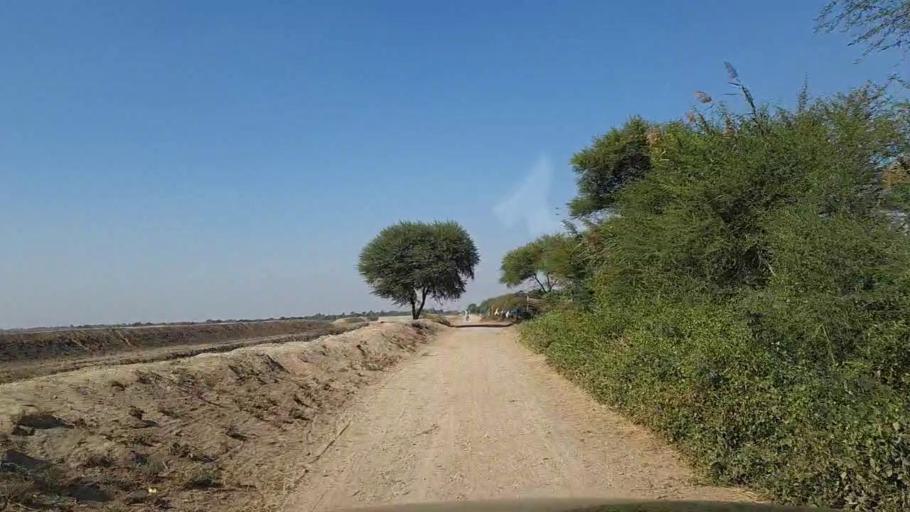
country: PK
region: Sindh
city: Mirpur Batoro
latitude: 24.7214
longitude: 68.2341
